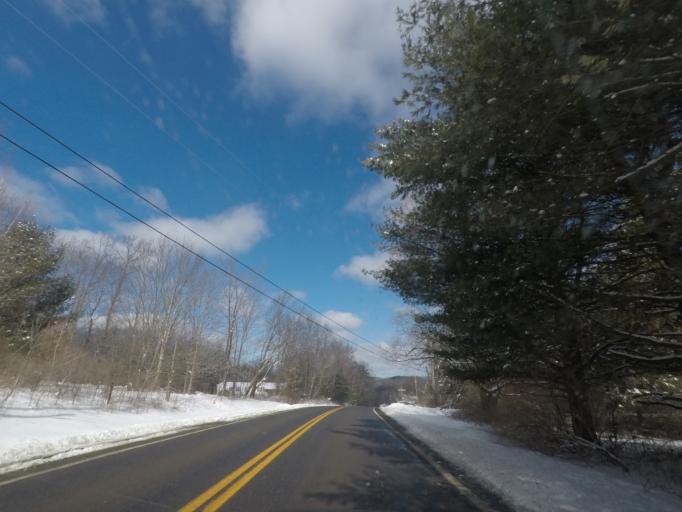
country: US
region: New York
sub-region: Rensselaer County
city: Nassau
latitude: 42.4823
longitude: -73.5204
